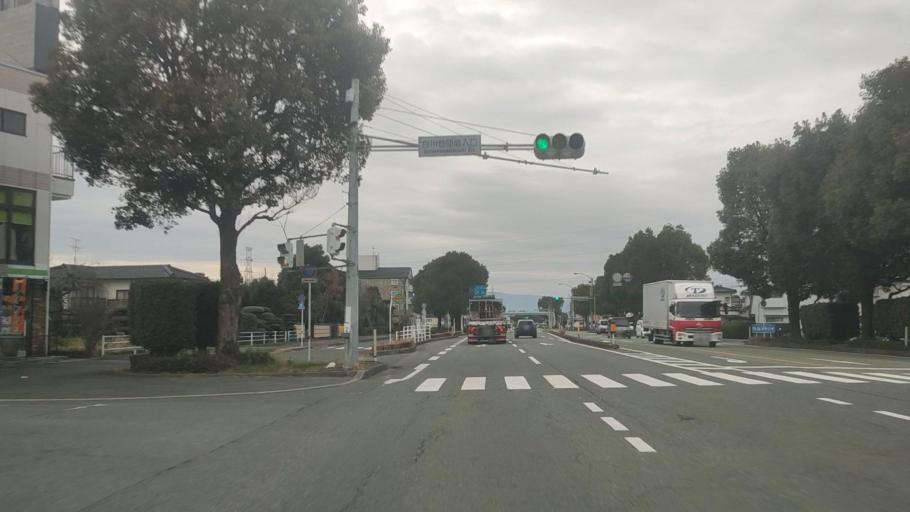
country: JP
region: Kumamoto
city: Ozu
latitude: 32.8556
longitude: 130.7868
